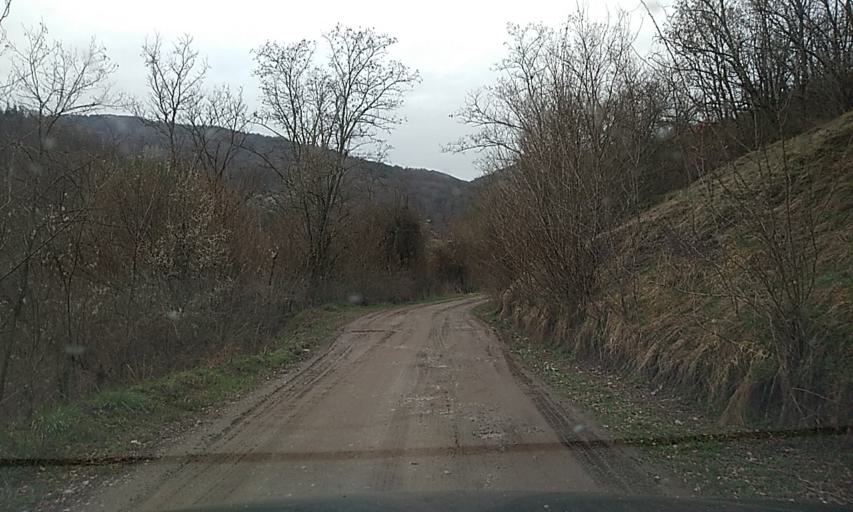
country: MK
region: Kriva Palanka
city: Kriva Palanka
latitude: 42.3506
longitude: 22.4009
